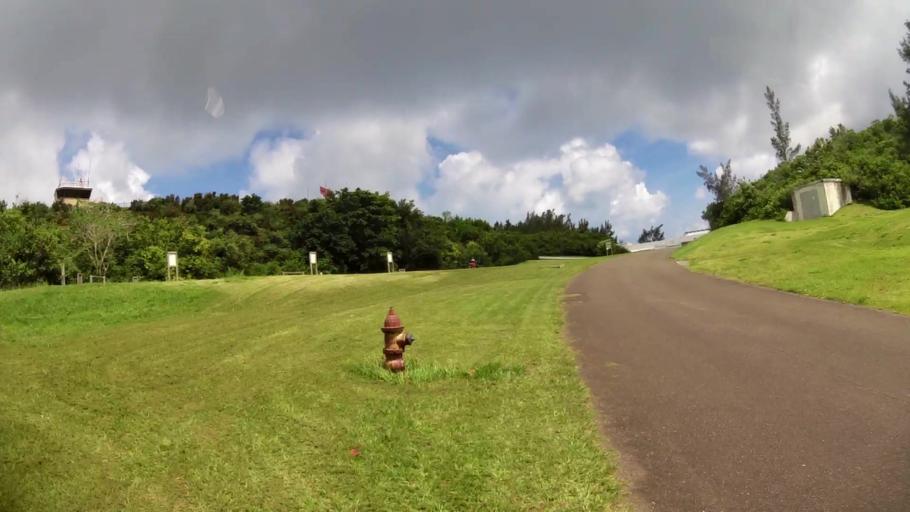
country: BM
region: Saint George
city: Saint George
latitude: 32.3668
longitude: -64.6764
